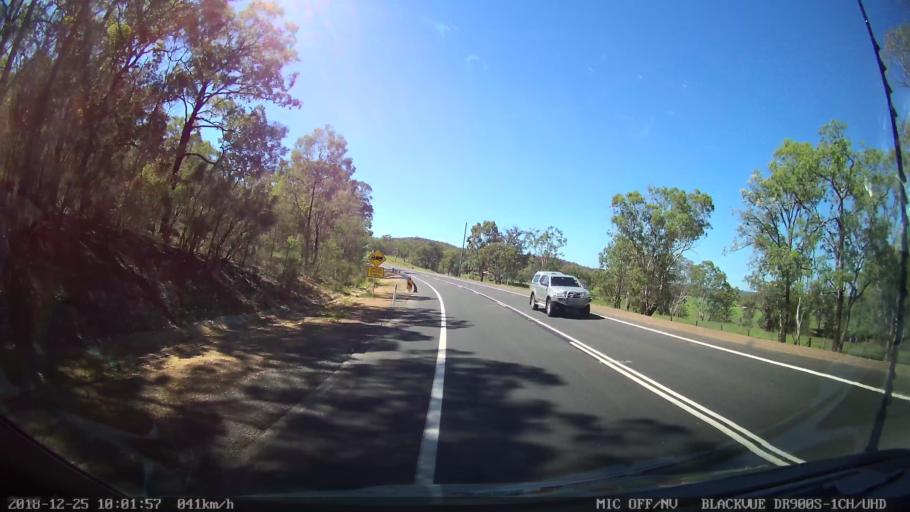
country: AU
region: New South Wales
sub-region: Upper Hunter Shire
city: Merriwa
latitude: -32.2137
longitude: 150.4610
